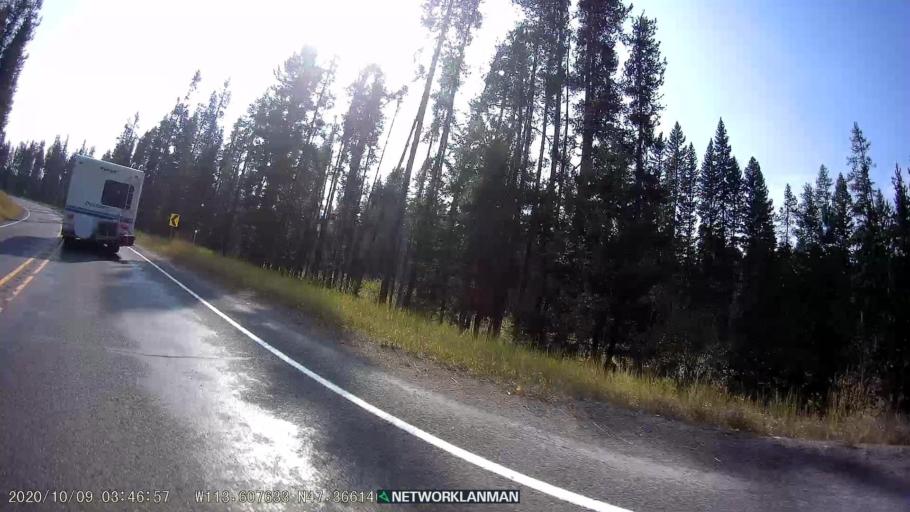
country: US
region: Montana
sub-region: Missoula County
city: Seeley Lake
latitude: 47.3661
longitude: -113.6072
